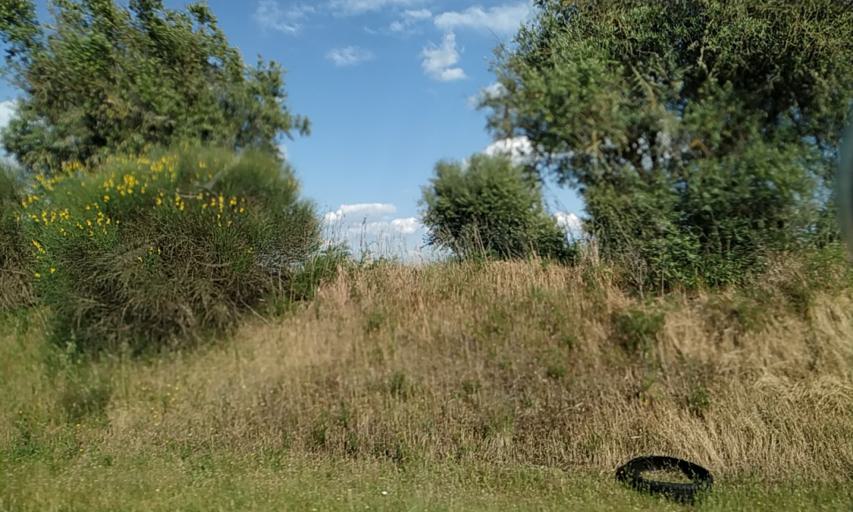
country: PT
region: Evora
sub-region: Estremoz
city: Estremoz
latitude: 38.9706
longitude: -7.4918
